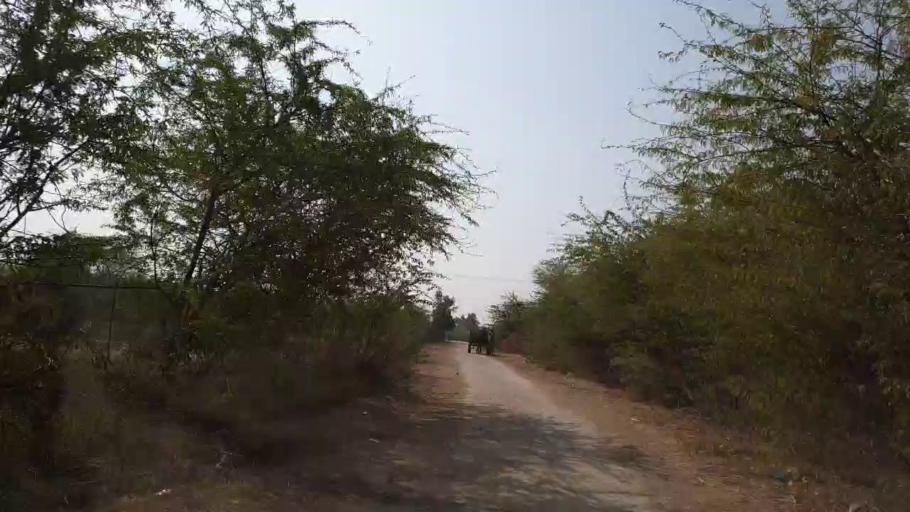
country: PK
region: Sindh
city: Mirpur Khas
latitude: 25.6040
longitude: 69.0220
